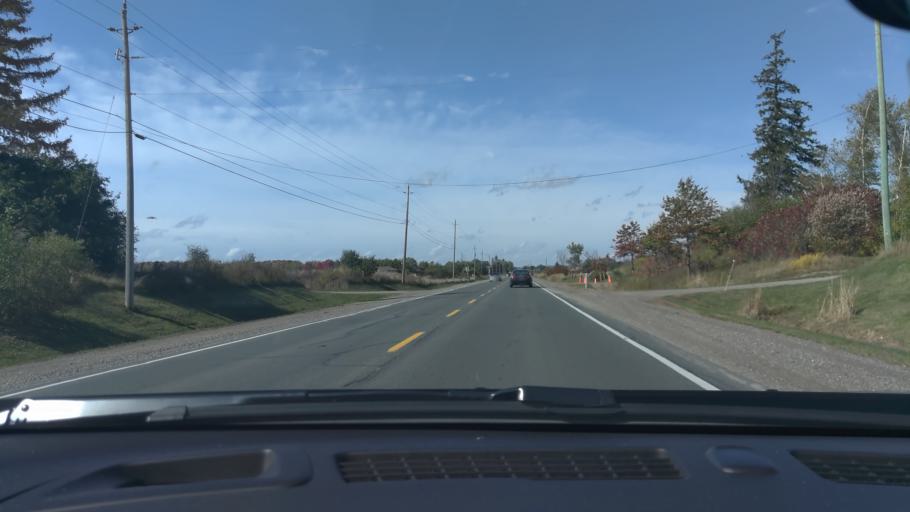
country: CA
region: Ontario
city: Brampton
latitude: 43.7959
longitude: -79.8377
